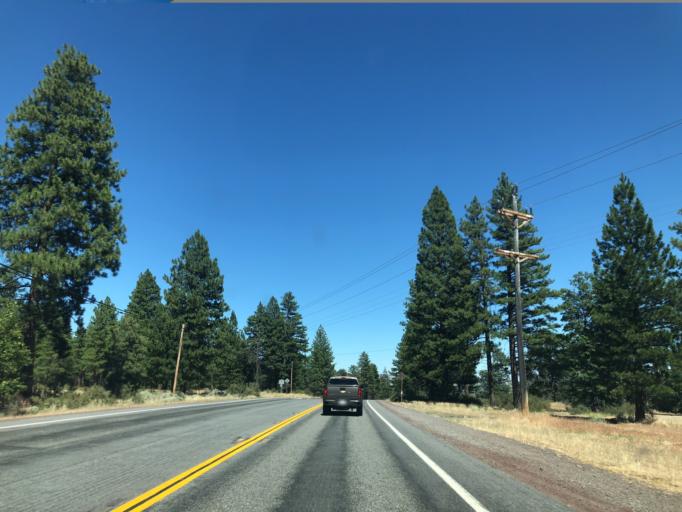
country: US
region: California
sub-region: Lassen County
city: Susanville
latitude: 40.4224
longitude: -120.6953
